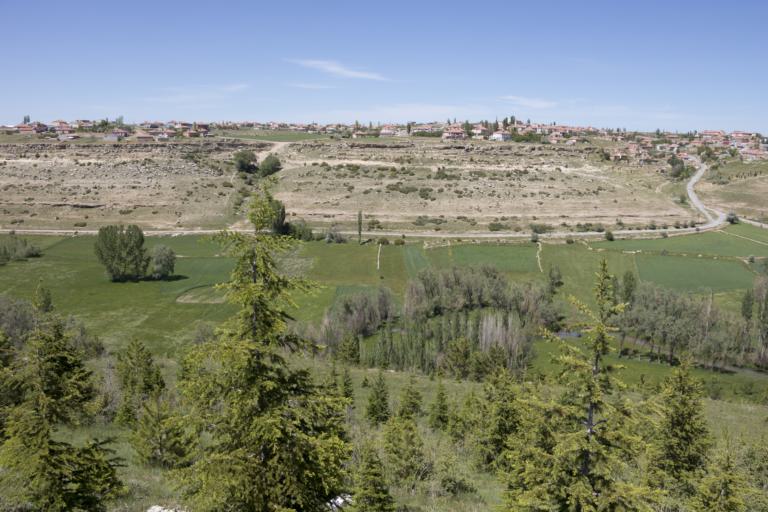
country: TR
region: Kayseri
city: Toklar
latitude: 38.4912
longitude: 36.1100
